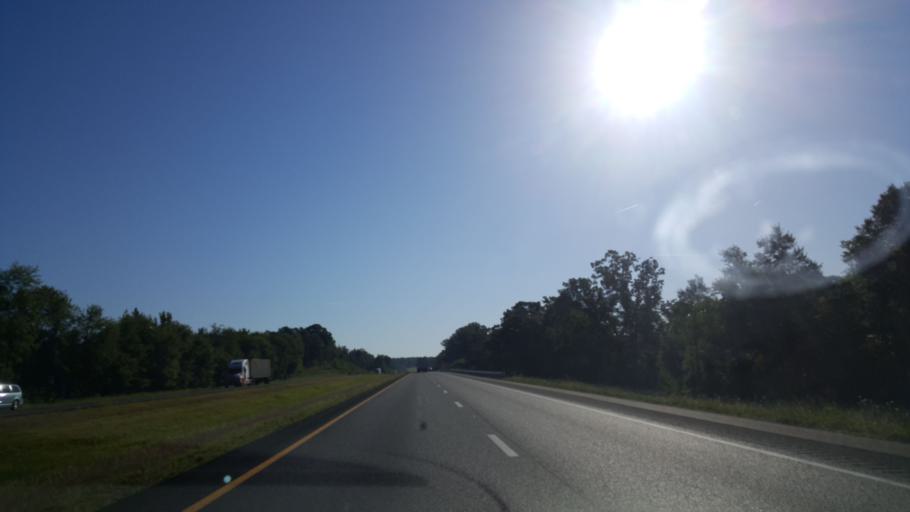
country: US
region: Tennessee
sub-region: Humphreys County
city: New Johnsonville
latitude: 35.8590
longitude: -88.0515
